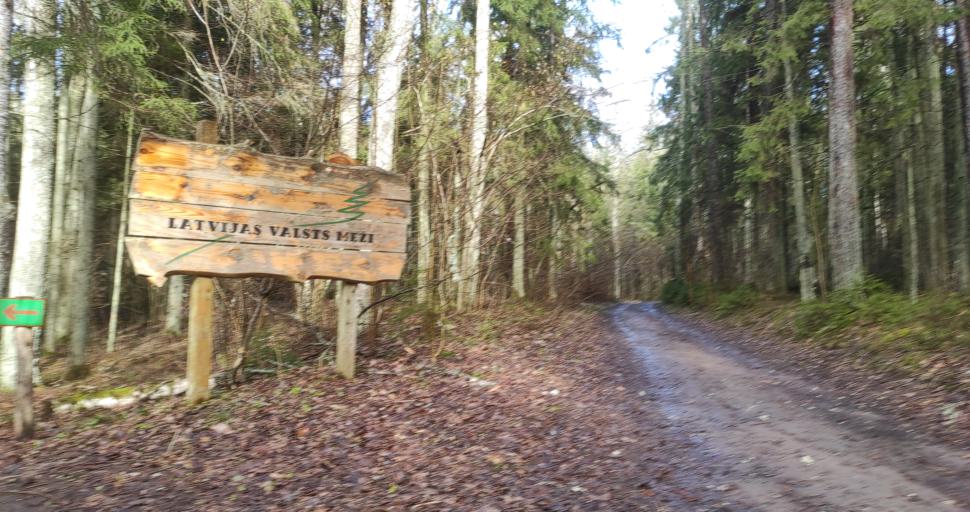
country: LV
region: Tukuma Rajons
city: Tukums
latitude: 57.1131
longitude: 23.0388
